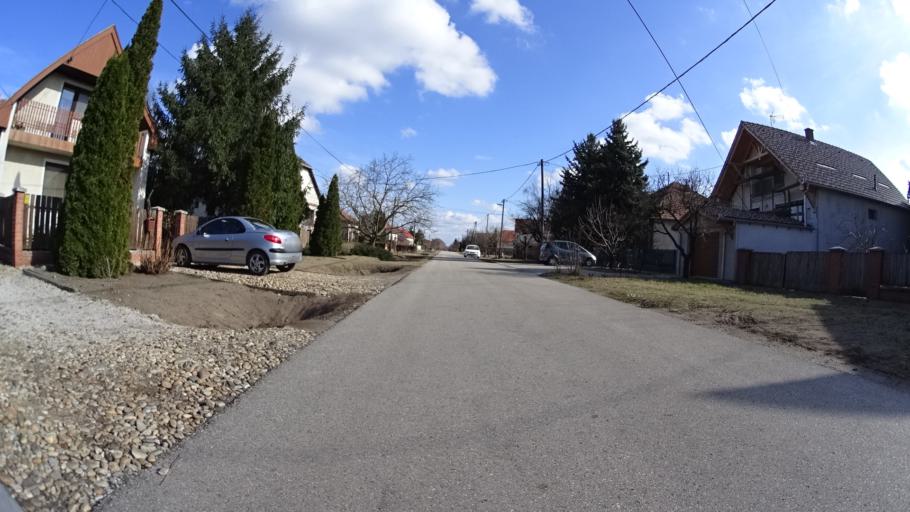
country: HU
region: Bacs-Kiskun
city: Tiszakecske
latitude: 46.9418
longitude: 20.0860
